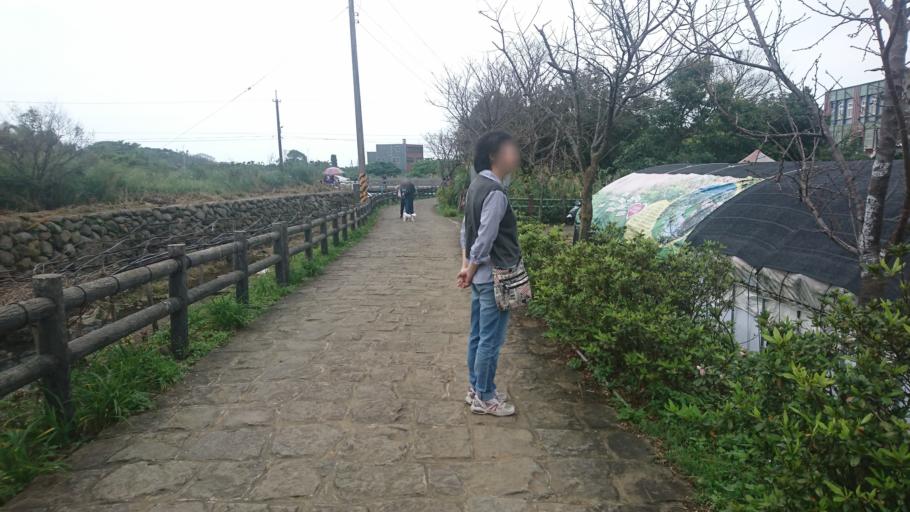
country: TW
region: Taipei
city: Taipei
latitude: 25.2678
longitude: 121.5109
